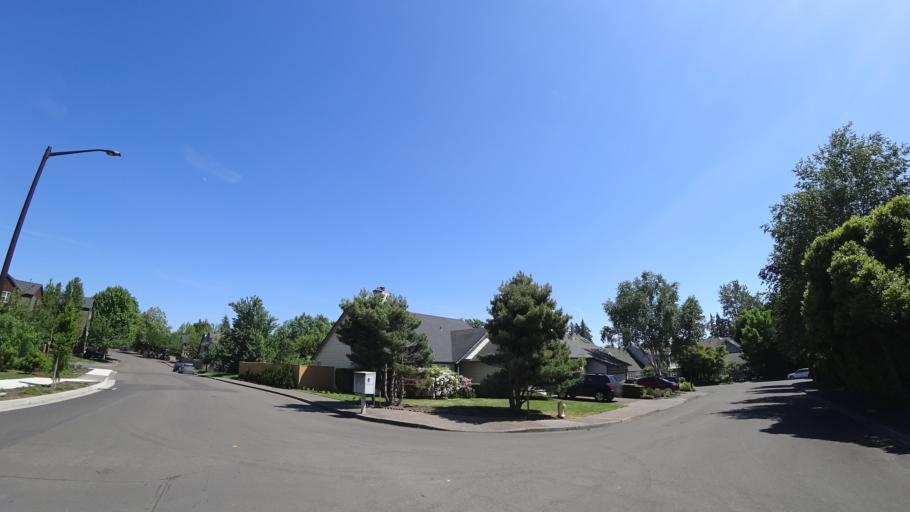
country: US
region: Oregon
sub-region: Washington County
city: King City
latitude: 45.4405
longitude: -122.8126
